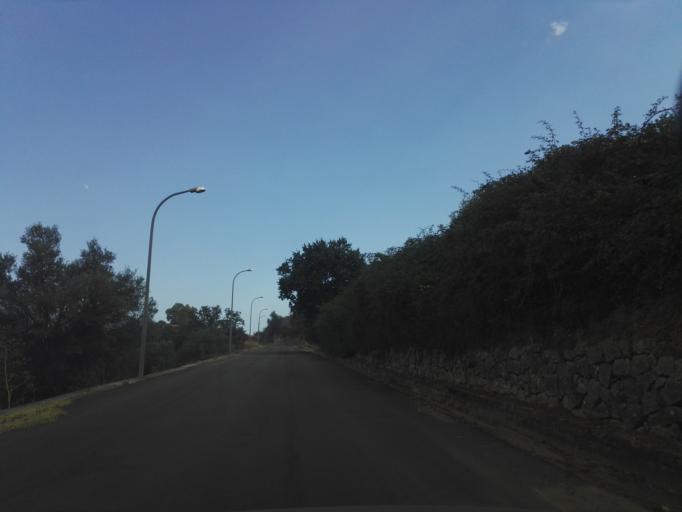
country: IT
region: Calabria
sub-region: Provincia di Reggio Calabria
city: Riace
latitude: 38.4138
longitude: 16.4856
